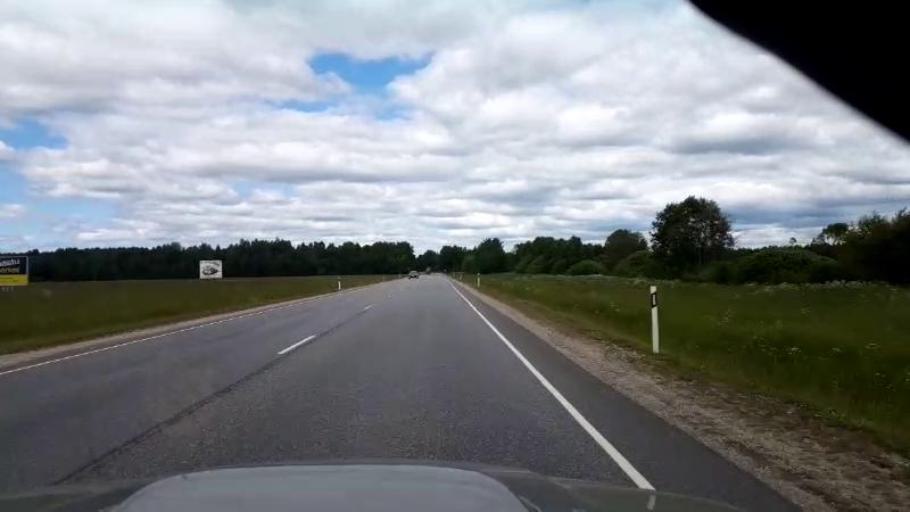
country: EE
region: Raplamaa
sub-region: Maerjamaa vald
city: Marjamaa
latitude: 58.9425
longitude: 24.4669
